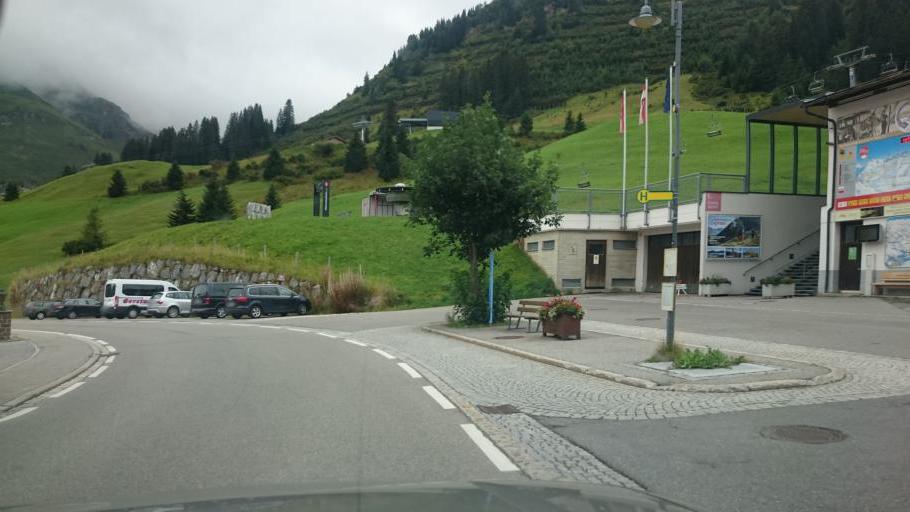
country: AT
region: Vorarlberg
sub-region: Politischer Bezirk Bregenz
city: Warth
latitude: 47.2603
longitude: 10.1764
